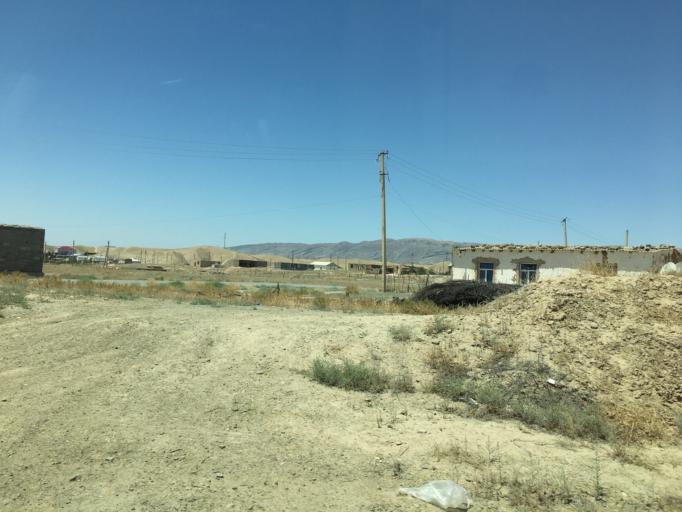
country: TM
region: Balkan
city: Magtymguly
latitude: 38.4356
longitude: 56.3200
